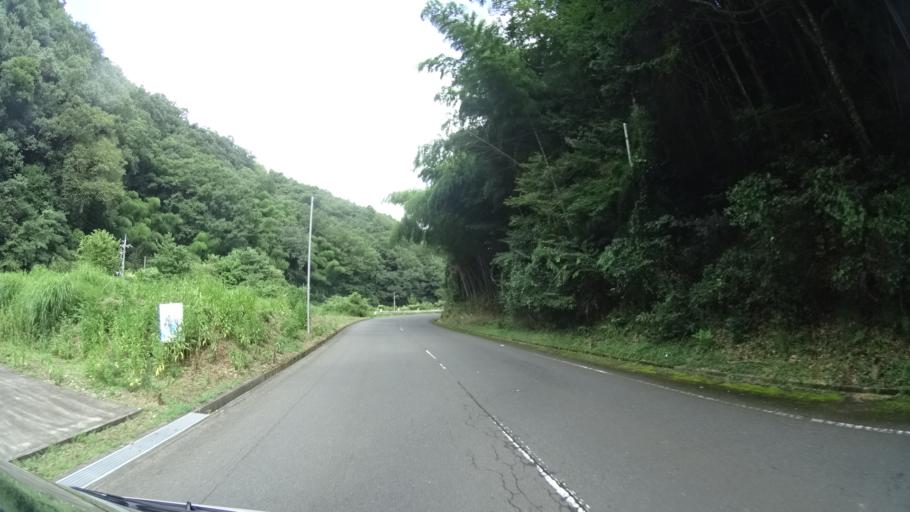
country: JP
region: Kyoto
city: Fukuchiyama
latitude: 35.3579
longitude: 135.1418
